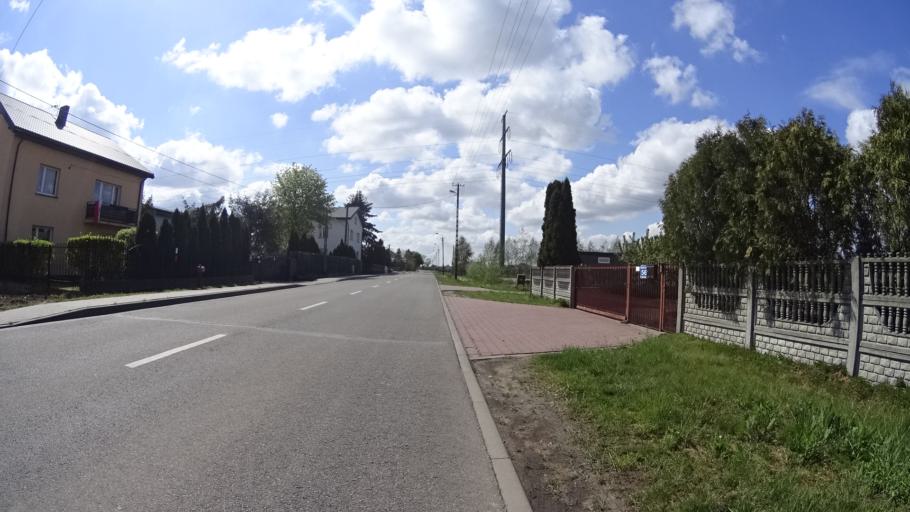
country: PL
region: Masovian Voivodeship
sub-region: Powiat warszawski zachodni
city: Ozarow Mazowiecki
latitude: 52.2309
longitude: 20.7430
